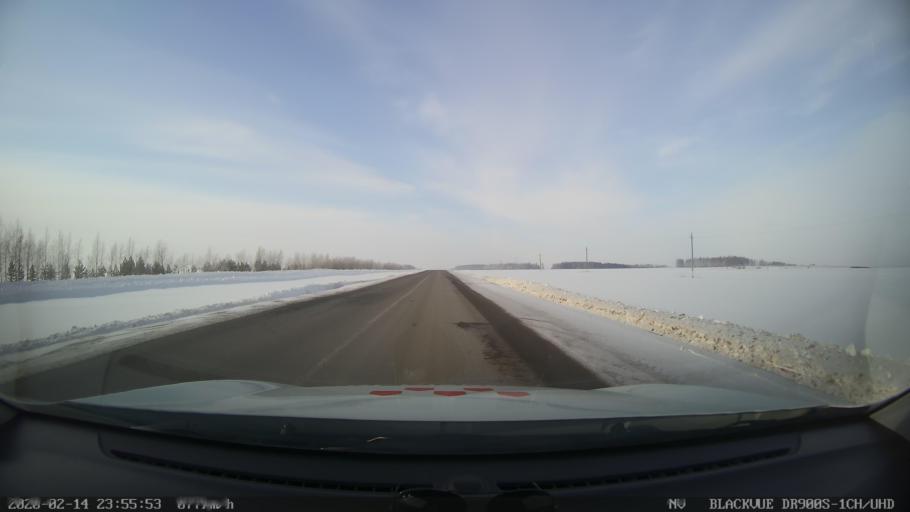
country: RU
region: Tatarstan
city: Kuybyshevskiy Zaton
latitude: 55.3194
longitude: 49.1389
